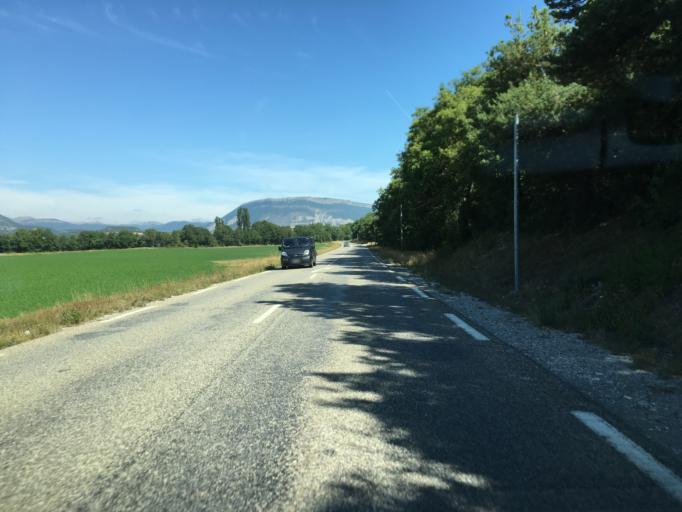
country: FR
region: Provence-Alpes-Cote d'Azur
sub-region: Departement des Hautes-Alpes
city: Serres
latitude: 44.4555
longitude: 5.7256
